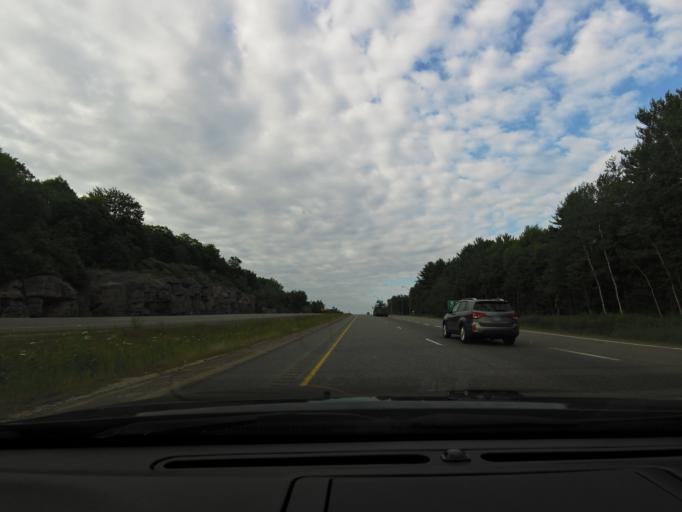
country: CA
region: Ontario
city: Bracebridge
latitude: 45.0168
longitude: -79.2951
